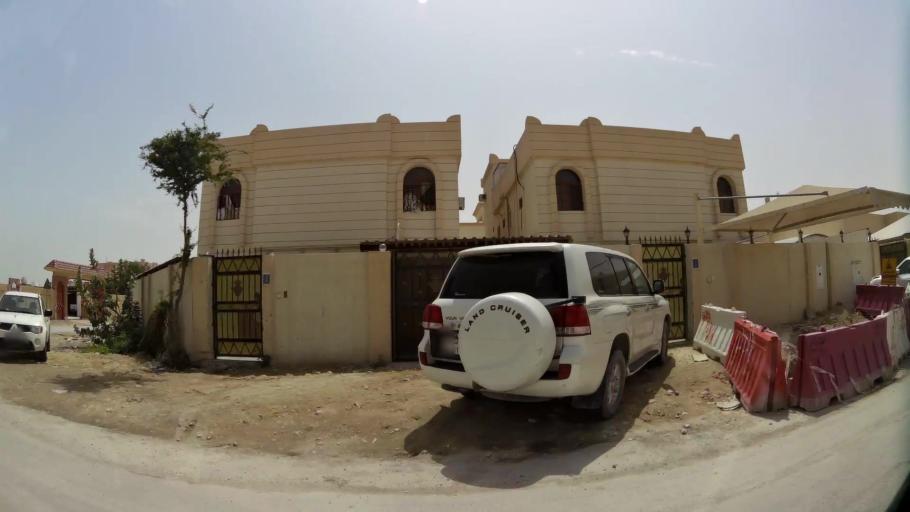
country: QA
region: Baladiyat ar Rayyan
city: Ar Rayyan
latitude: 25.2369
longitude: 51.4169
